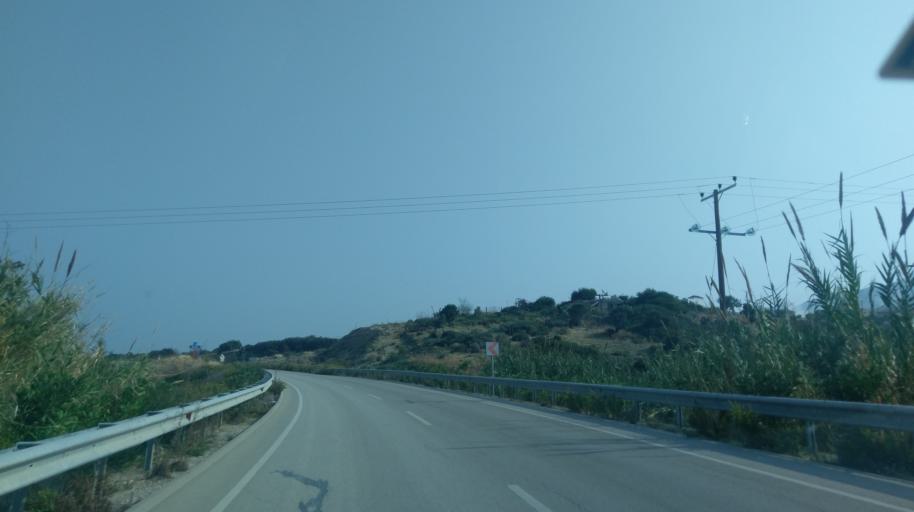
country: CY
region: Ammochostos
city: Trikomo
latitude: 35.4236
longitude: 33.8993
